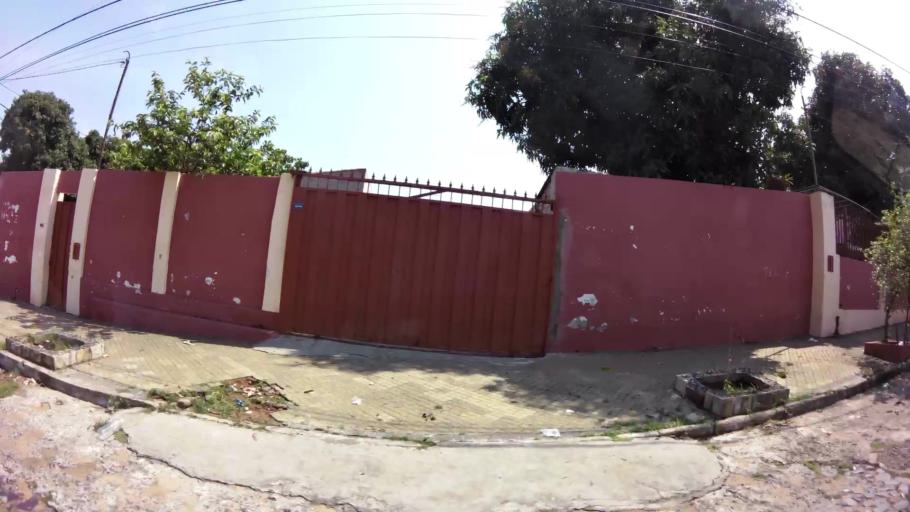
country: PY
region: Presidente Hayes
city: Nanawa
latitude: -25.2816
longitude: -57.6534
